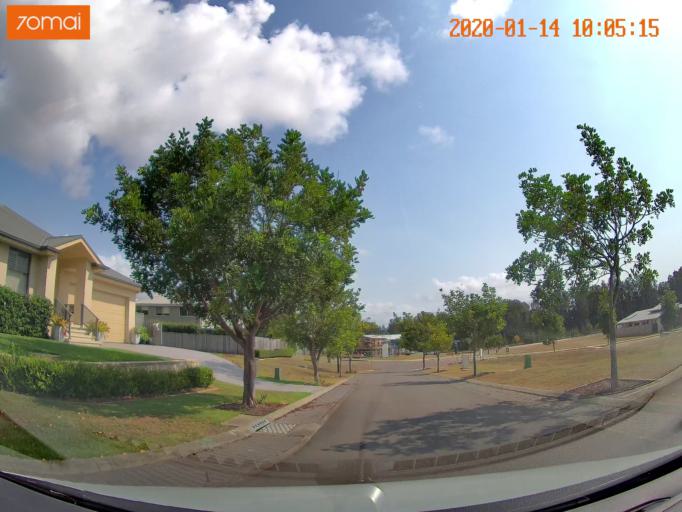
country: AU
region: New South Wales
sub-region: Wyong Shire
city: Kingfisher Shores
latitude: -33.1249
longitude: 151.5372
